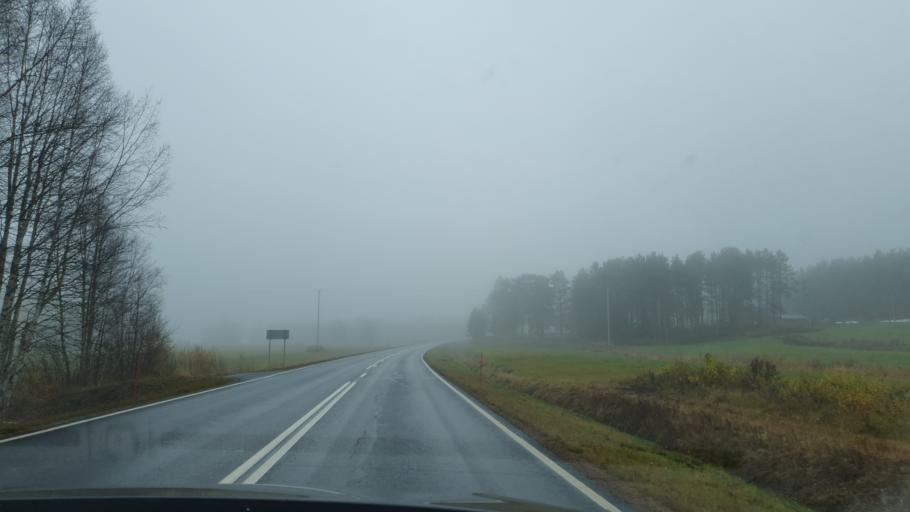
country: FI
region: Lapland
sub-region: Rovaniemi
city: Rovaniemi
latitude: 66.8081
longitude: 25.4105
